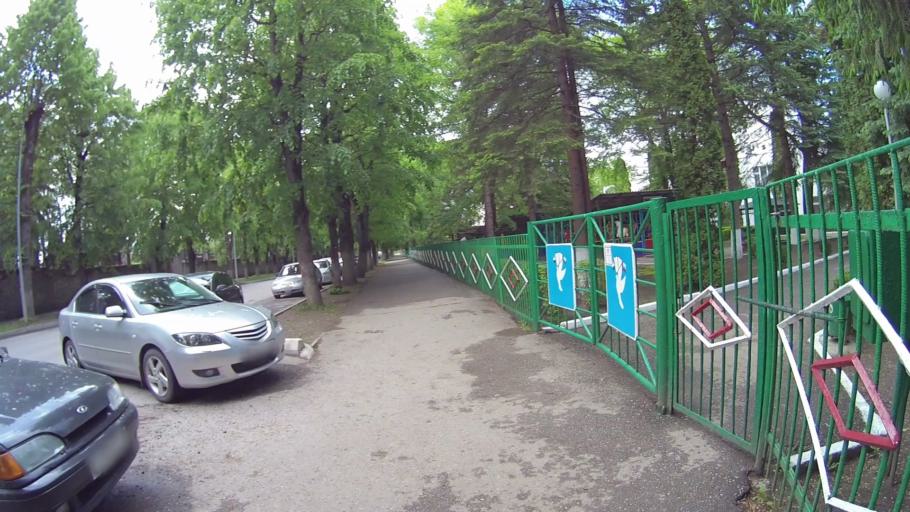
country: RU
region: Kabardino-Balkariya
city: Vol'nyy Aul
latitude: 43.4682
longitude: 43.5863
